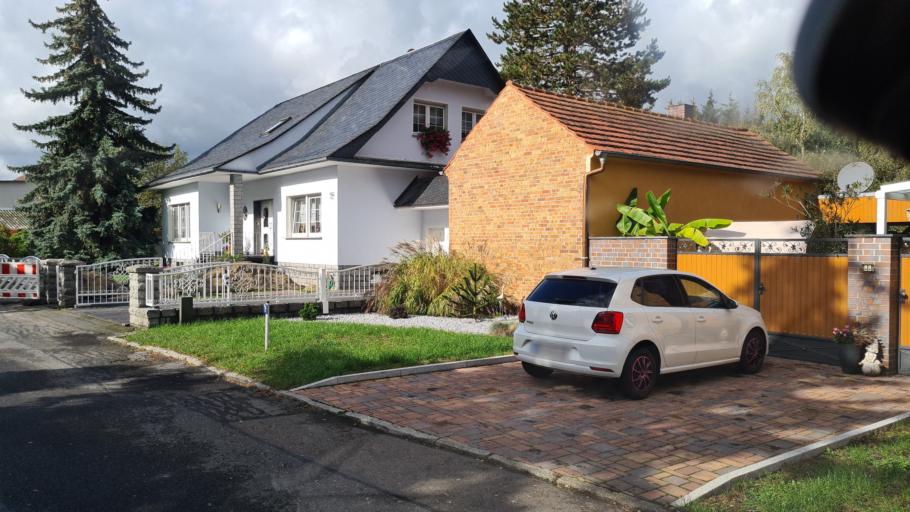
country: DE
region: Brandenburg
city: Grossraschen
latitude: 51.5842
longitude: 13.9625
